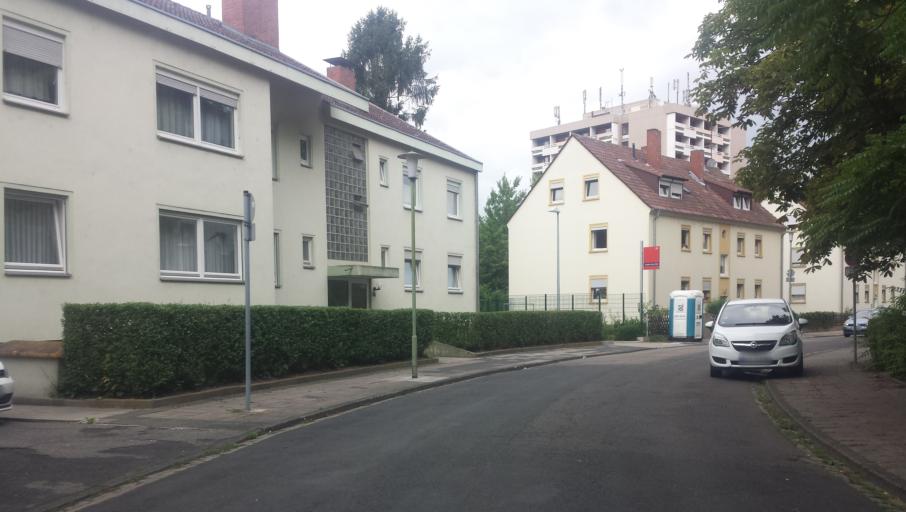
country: DE
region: Rheinland-Pfalz
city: Landau in der Pfalz
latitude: 49.1881
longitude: 8.1158
